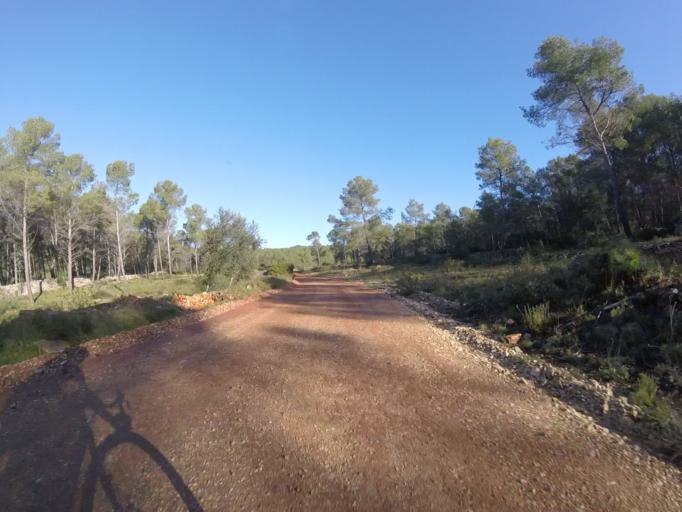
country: ES
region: Valencia
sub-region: Provincia de Castello
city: Alcala de Xivert
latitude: 40.3075
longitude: 0.2755
